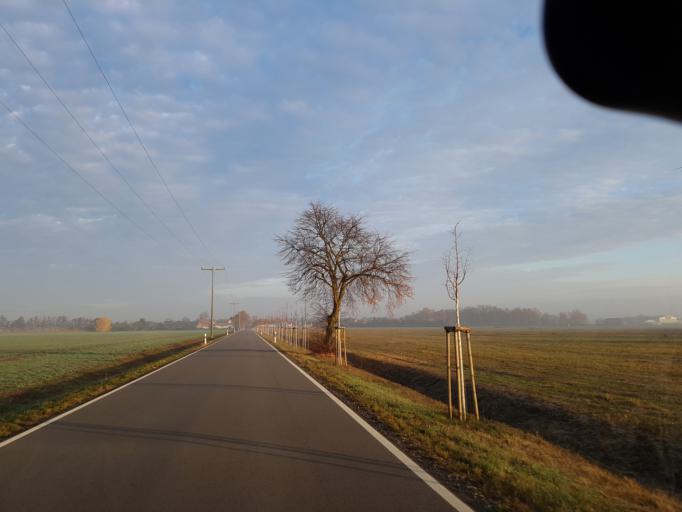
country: DE
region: Saxony-Anhalt
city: Elster
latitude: 51.8591
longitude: 12.8452
